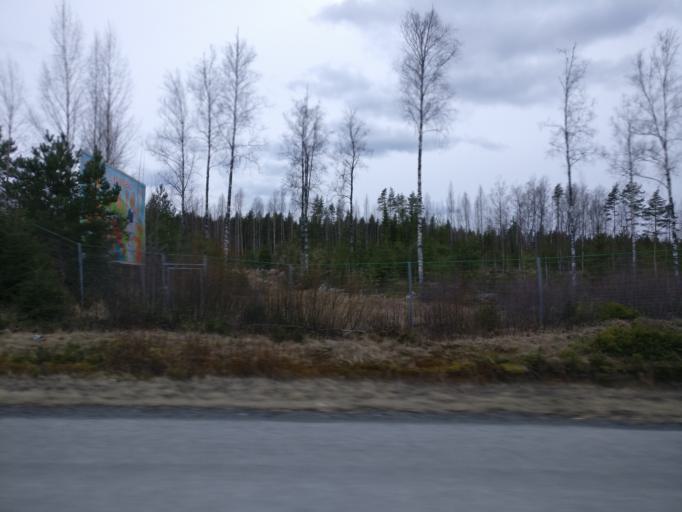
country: FI
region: Haeme
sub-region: Haemeenlinna
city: Kalvola
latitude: 61.1140
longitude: 24.1349
